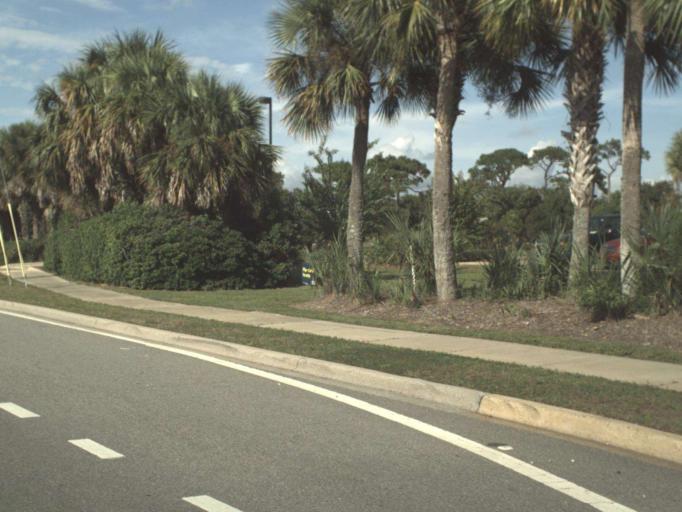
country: US
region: Florida
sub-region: Gulf County
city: Port Saint Joe
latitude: 29.8160
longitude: -85.3050
